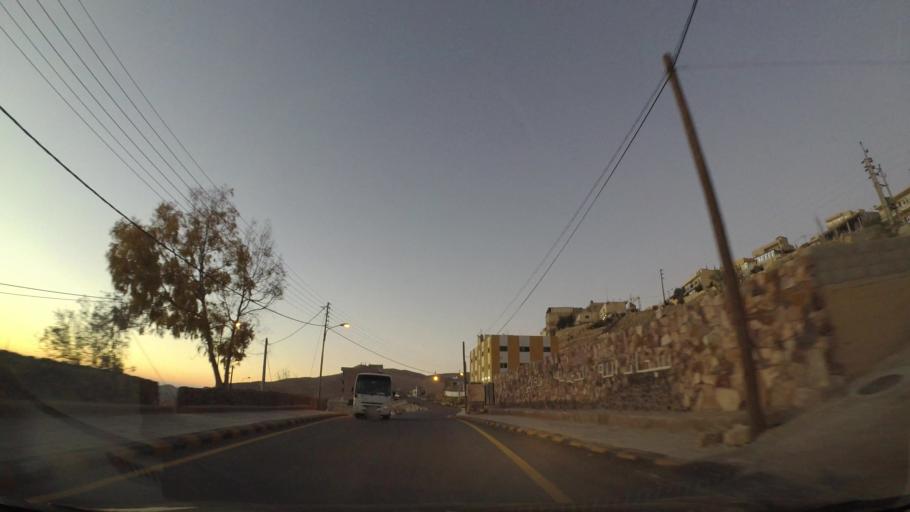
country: JO
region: Ma'an
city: Petra
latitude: 30.3201
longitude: 35.4825
